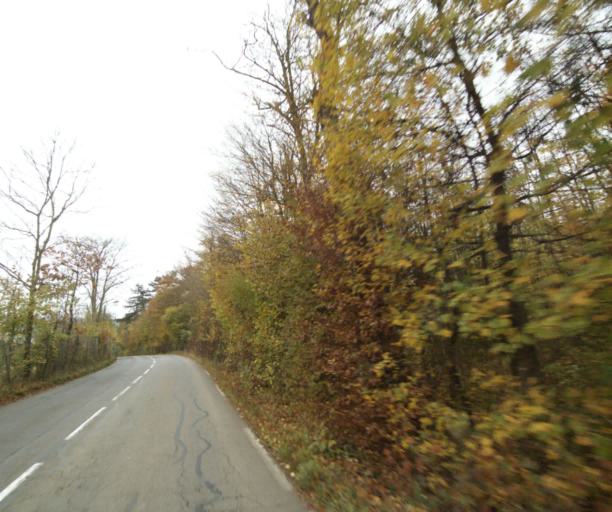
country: FR
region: Lorraine
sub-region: Departement de Meurthe-et-Moselle
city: Joeuf
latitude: 49.2355
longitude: 6.0271
